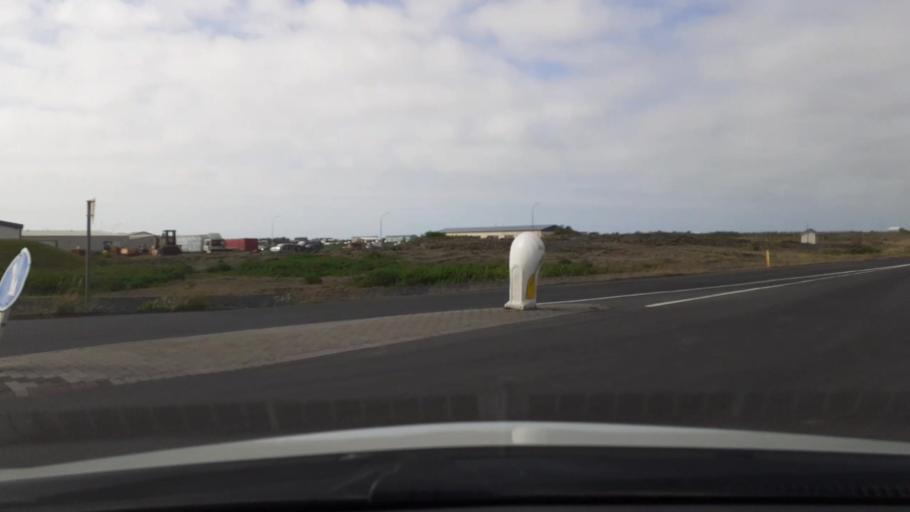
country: IS
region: South
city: THorlakshoefn
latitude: 63.8636
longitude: -21.3822
